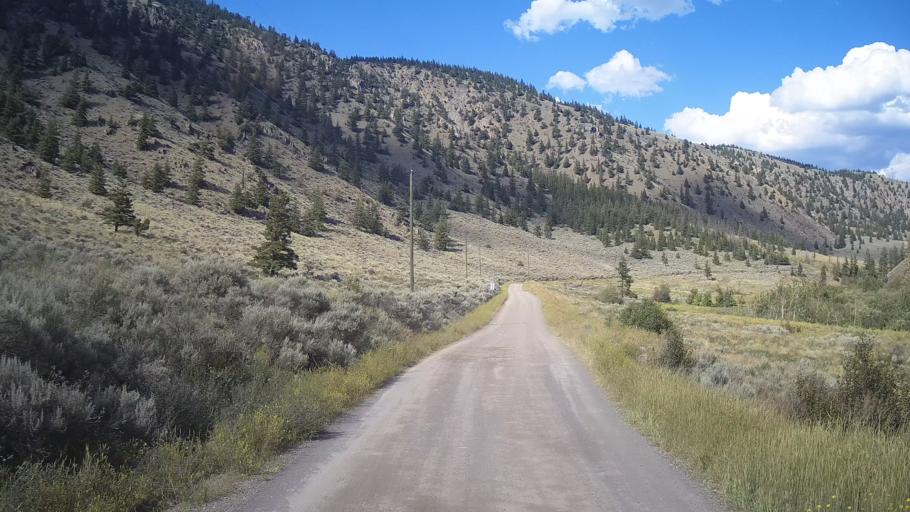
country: CA
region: British Columbia
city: Lillooet
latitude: 51.2161
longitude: -122.0946
